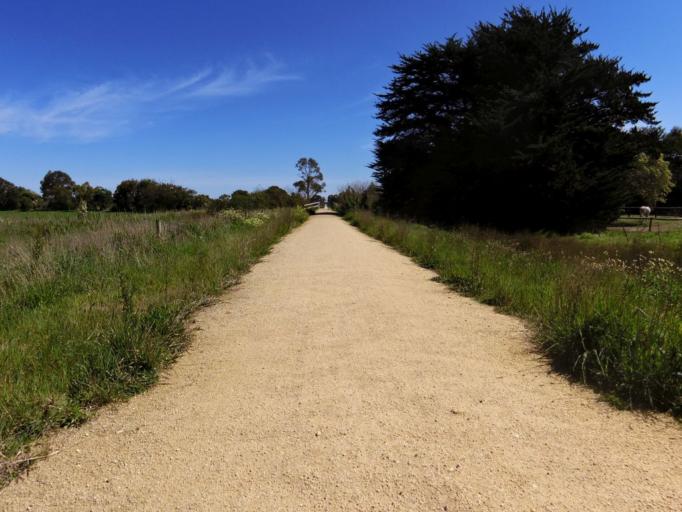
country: AU
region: Victoria
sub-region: Latrobe
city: Morwell
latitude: -38.6665
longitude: 146.4362
